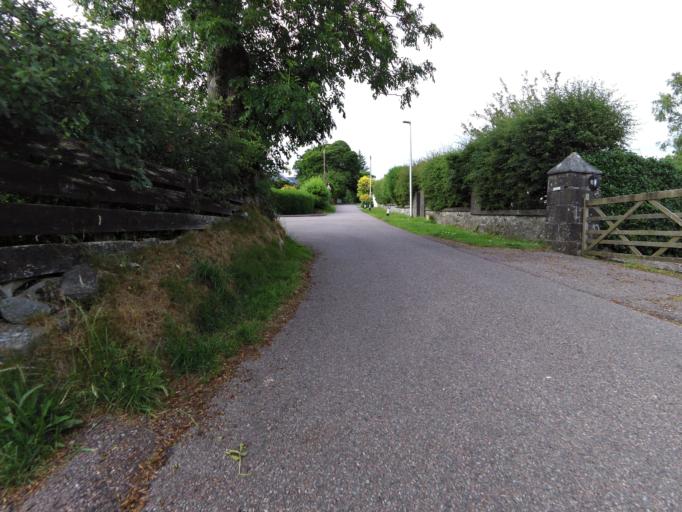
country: GB
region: Scotland
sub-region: Argyll and Bute
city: Isle Of Mull
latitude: 56.9103
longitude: -5.8427
